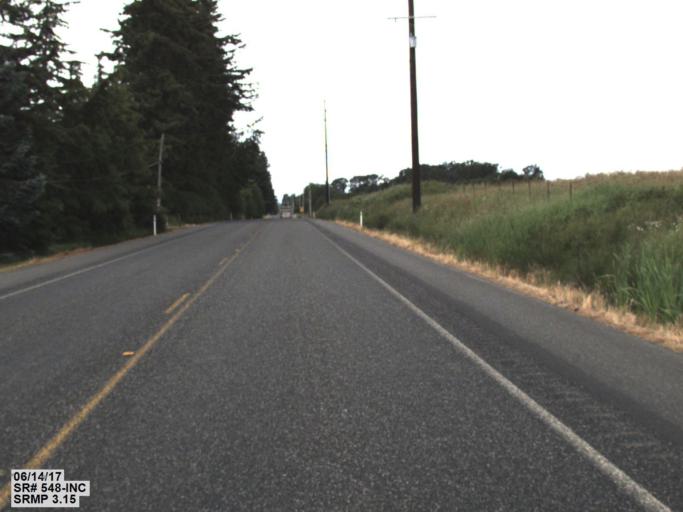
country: US
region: Washington
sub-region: Whatcom County
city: Birch Bay
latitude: 48.8919
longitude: -122.6653
